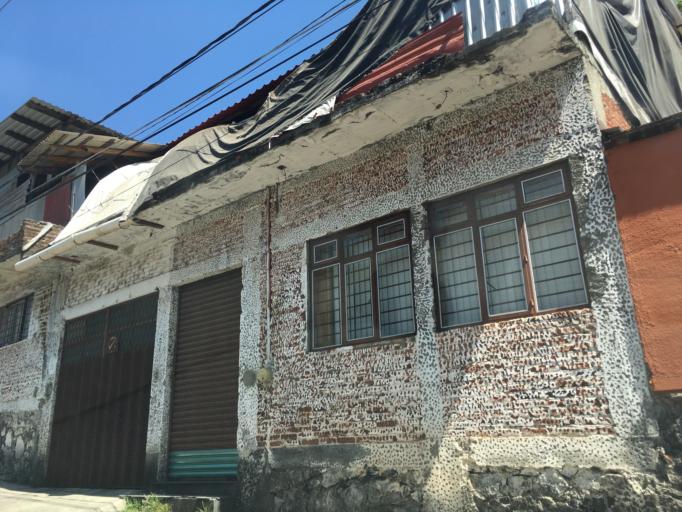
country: MX
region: Michoacan
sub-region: Uruapan
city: Uruapan
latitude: 19.4167
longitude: -102.0676
